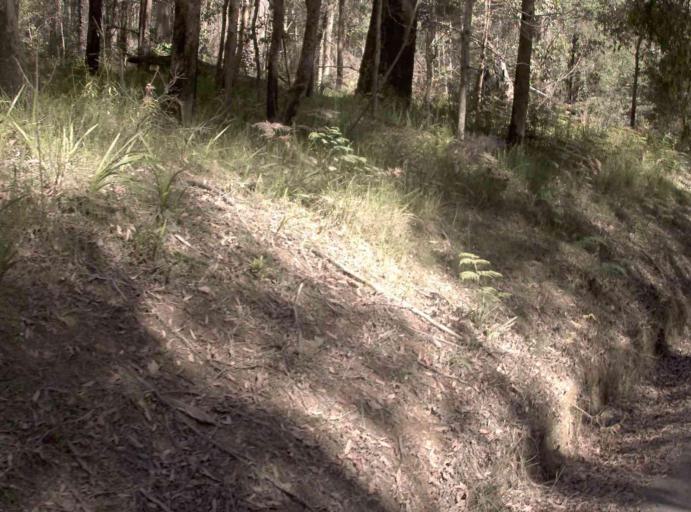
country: AU
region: New South Wales
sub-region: Bombala
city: Bombala
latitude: -37.2128
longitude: 148.7458
